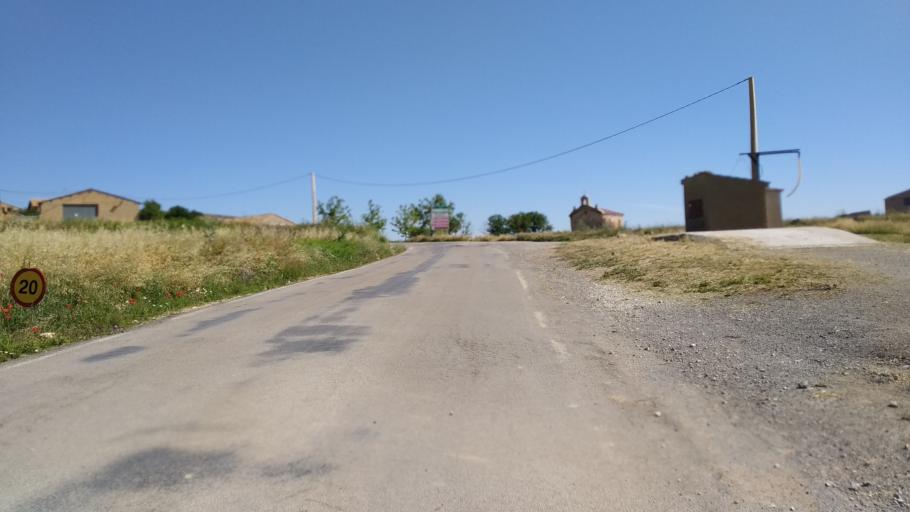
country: ES
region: Aragon
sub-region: Provincia de Teruel
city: Monforte de Moyuela
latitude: 41.0537
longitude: -1.0127
